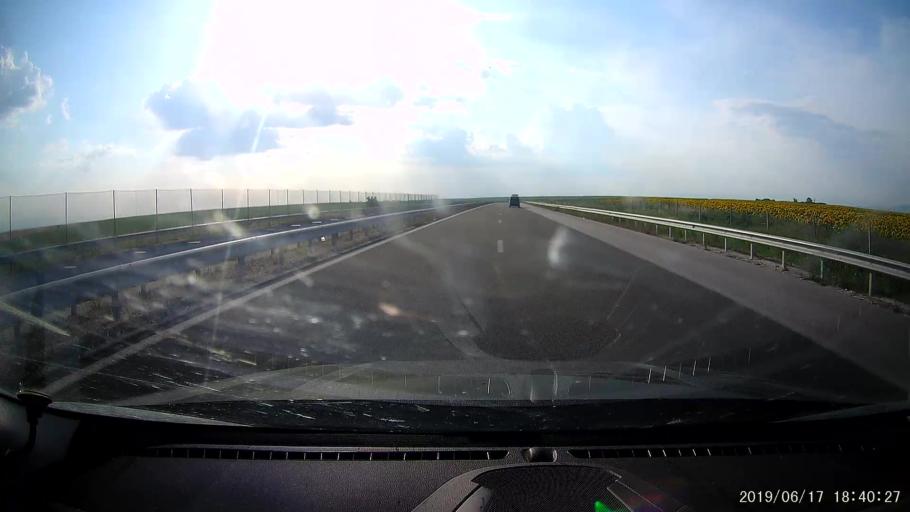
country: BG
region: Stara Zagora
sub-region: Obshtina Chirpan
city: Chirpan
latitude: 42.1556
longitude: 25.2777
